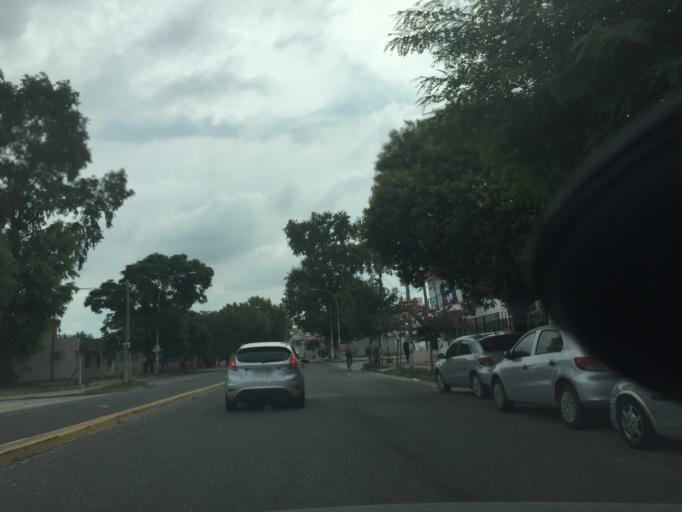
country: AR
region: Cordoba
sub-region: Departamento de Capital
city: Cordoba
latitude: -31.4509
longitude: -64.2016
